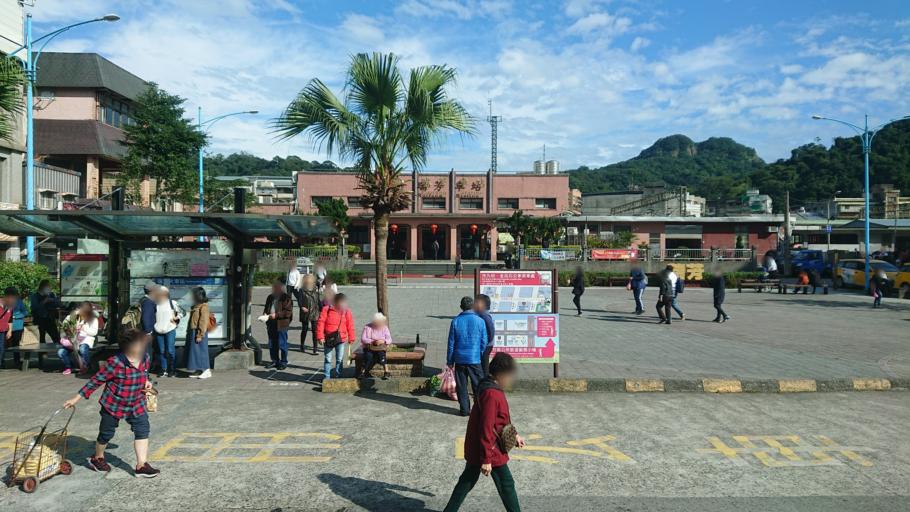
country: TW
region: Taiwan
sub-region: Keelung
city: Keelung
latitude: 25.1082
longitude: 121.8059
